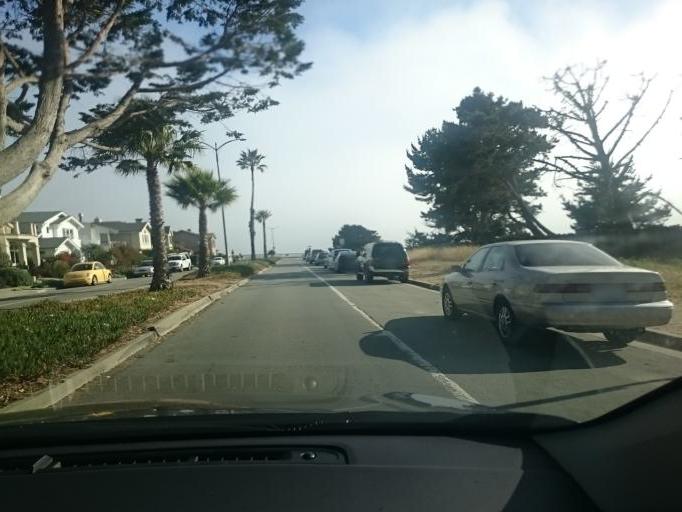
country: US
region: California
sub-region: Santa Cruz County
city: Santa Cruz
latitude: 36.9510
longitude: -122.0551
